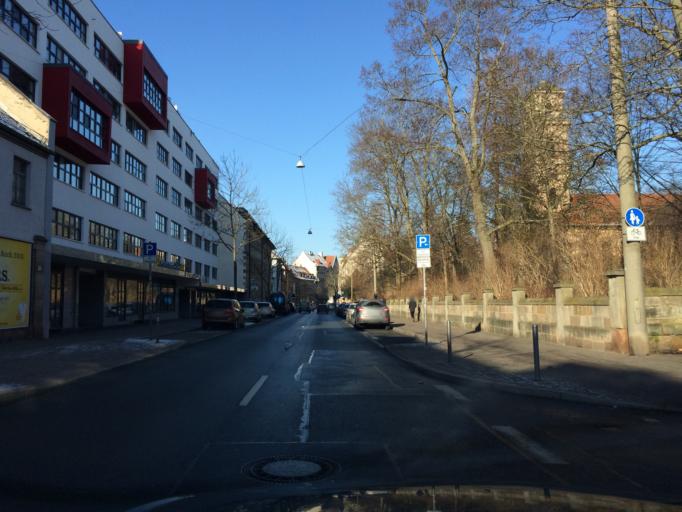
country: DE
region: Bavaria
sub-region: Regierungsbezirk Mittelfranken
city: Furth
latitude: 49.4711
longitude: 10.9966
